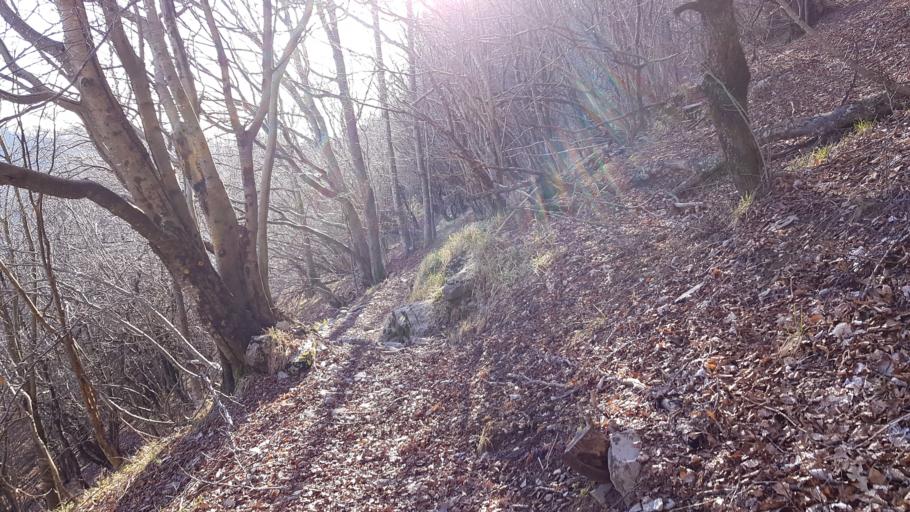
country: IT
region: Liguria
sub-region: Provincia di Genova
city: Torriglia
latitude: 44.5507
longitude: 9.1544
